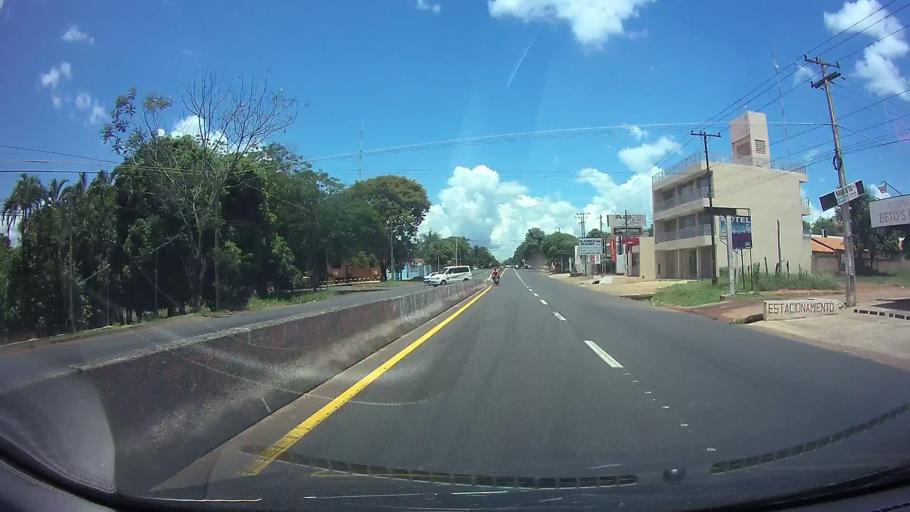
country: PY
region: Central
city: Itaugua
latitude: -25.3788
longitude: -57.3865
